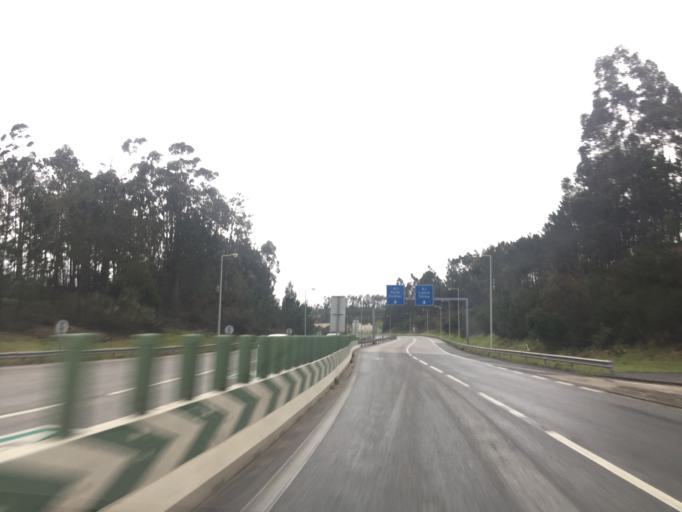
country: PT
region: Leiria
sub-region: Leiria
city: Caranguejeira
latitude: 39.7380
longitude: -8.7450
